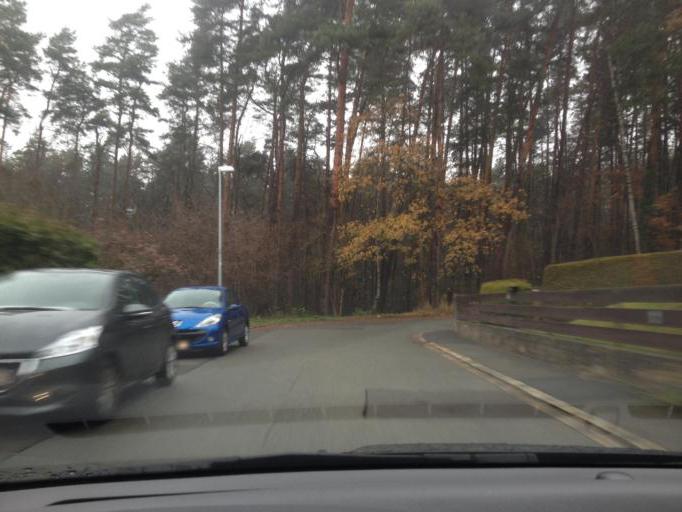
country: DE
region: Bavaria
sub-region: Regierungsbezirk Mittelfranken
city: Lauf an der Pegnitz
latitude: 49.5282
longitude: 11.2682
